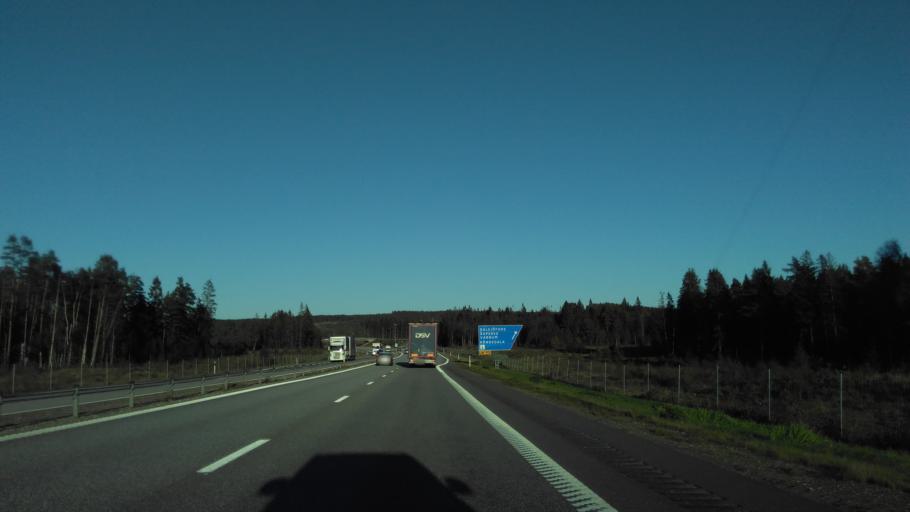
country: SE
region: Vaestra Goetaland
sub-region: Boras Kommun
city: Dalsjofors
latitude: 57.7557
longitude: 13.0920
